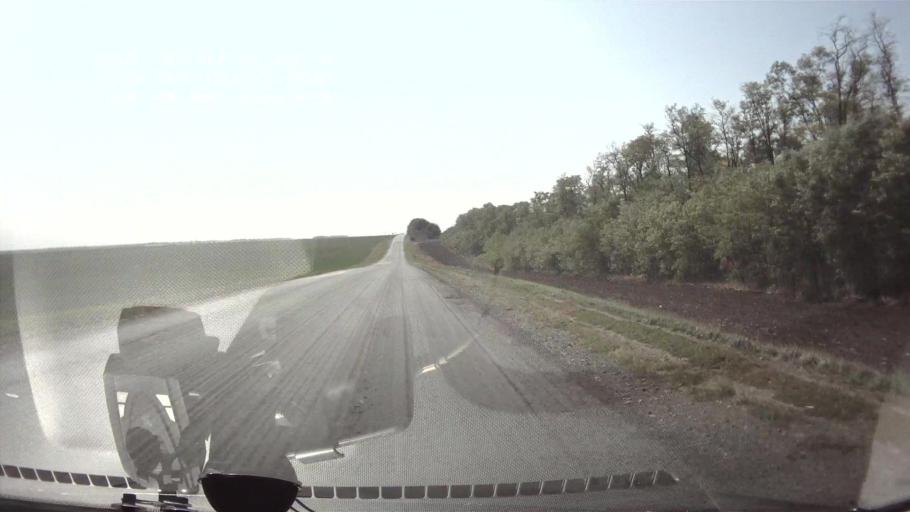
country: RU
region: Krasnodarskiy
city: Dmitriyevskaya
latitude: 45.6774
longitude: 40.7443
